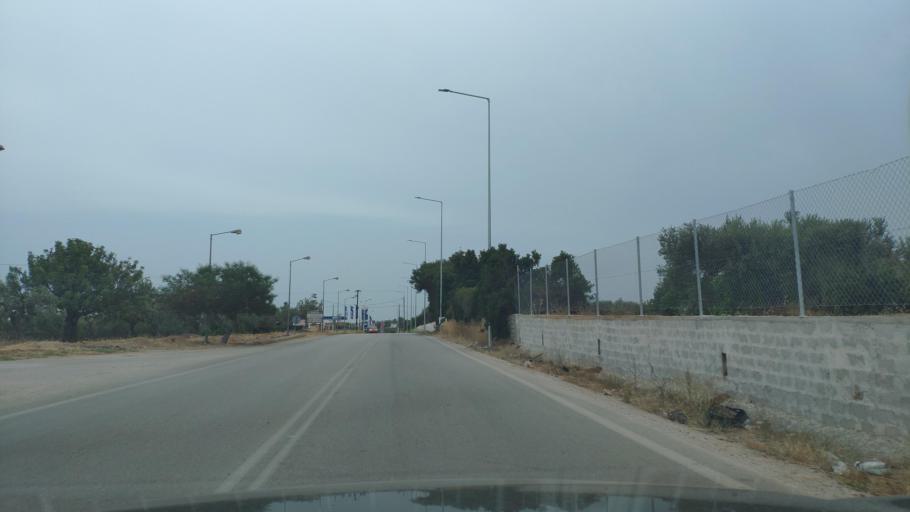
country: GR
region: Peloponnese
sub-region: Nomos Argolidos
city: Porto Cheli
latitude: 37.3460
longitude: 23.1575
